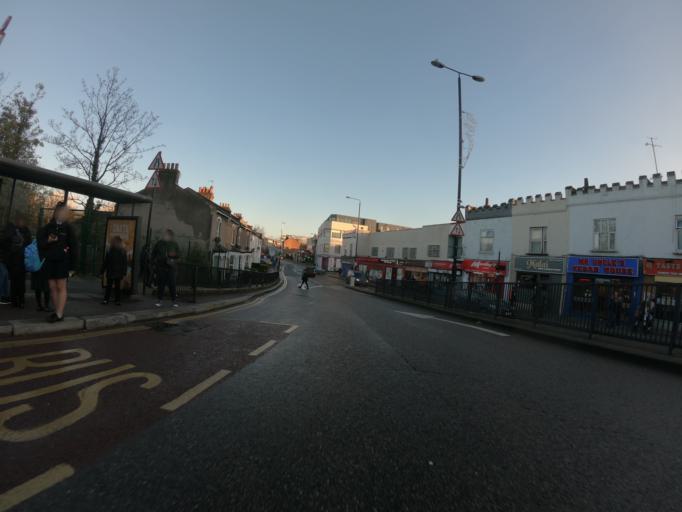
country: GB
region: England
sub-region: Greater London
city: Woolwich
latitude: 51.4895
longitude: 0.0859
